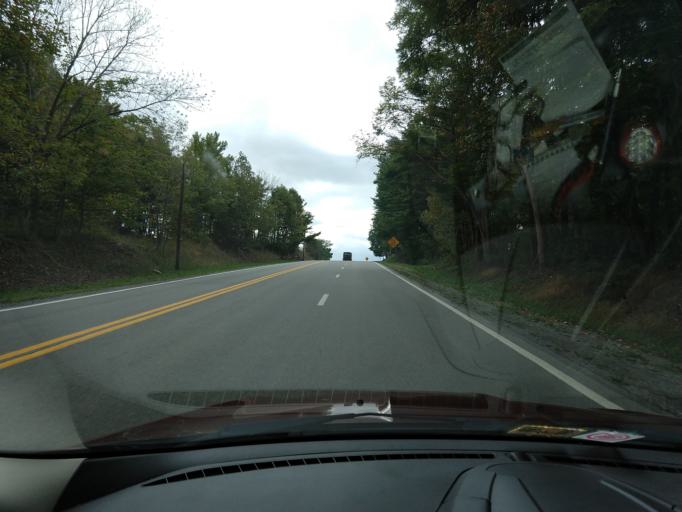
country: US
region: West Virginia
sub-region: Barbour County
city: Belington
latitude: 39.0648
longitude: -79.9751
